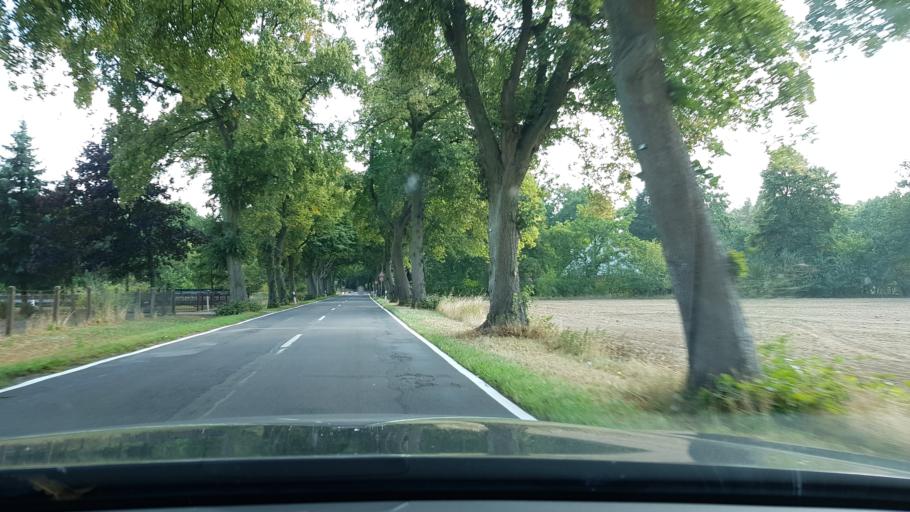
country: DE
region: Brandenburg
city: Lindow
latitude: 52.9826
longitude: 12.9813
